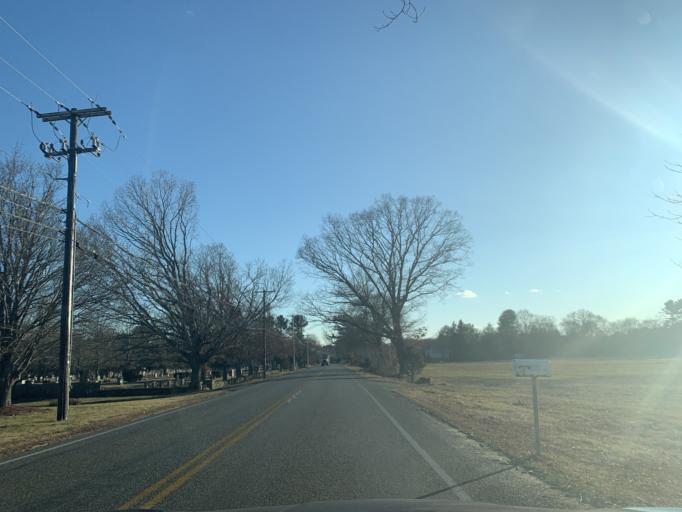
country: US
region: Massachusetts
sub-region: Bristol County
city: Rehoboth
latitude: 41.9024
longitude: -71.2185
